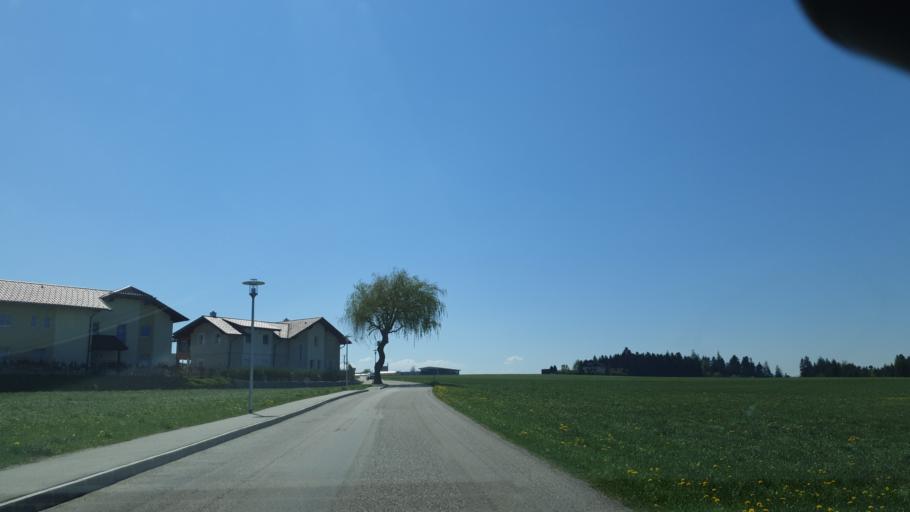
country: AT
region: Upper Austria
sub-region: Politischer Bezirk Vocklabruck
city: Gampern
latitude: 47.9851
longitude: 13.5499
